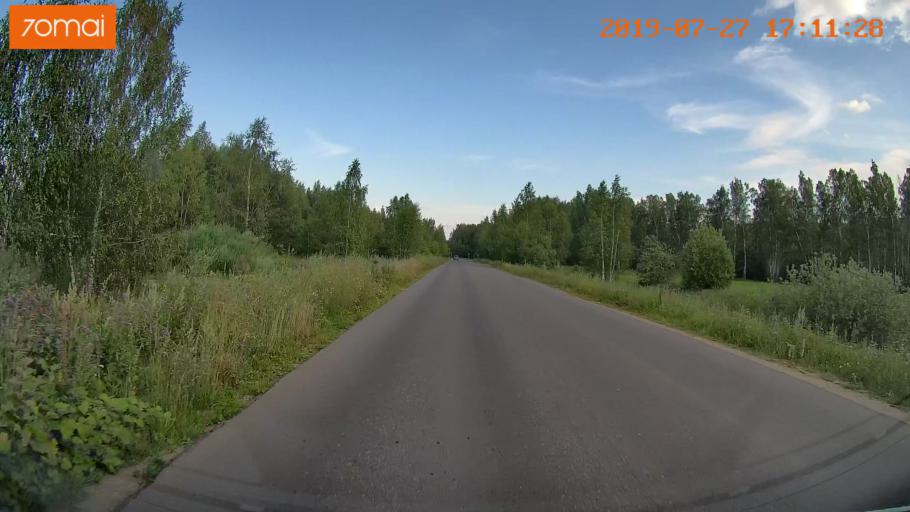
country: RU
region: Ivanovo
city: Novo-Talitsy
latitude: 57.0644
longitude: 40.8621
